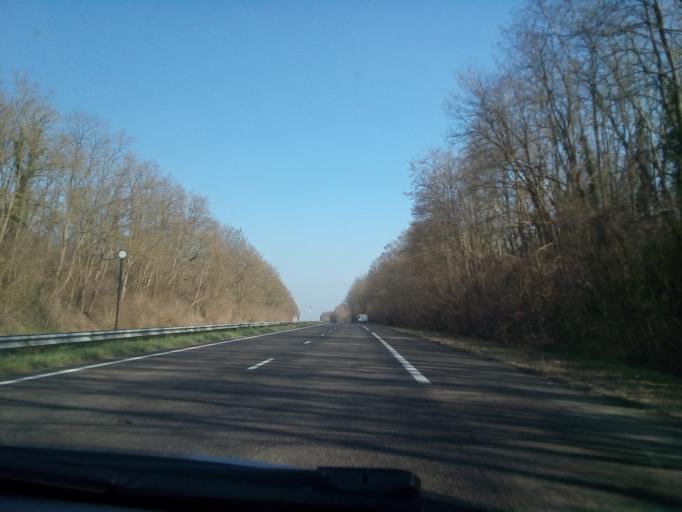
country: DE
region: Rheinland-Pfalz
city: Scheibenhardt
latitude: 48.9540
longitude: 8.1430
